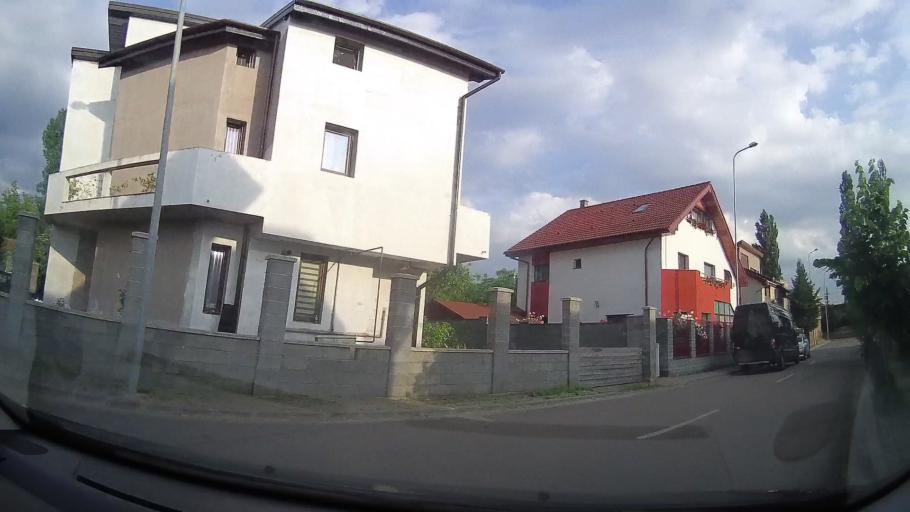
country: RO
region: Timis
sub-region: Comuna Dumbravita
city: Dumbravita
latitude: 45.7821
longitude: 21.2317
